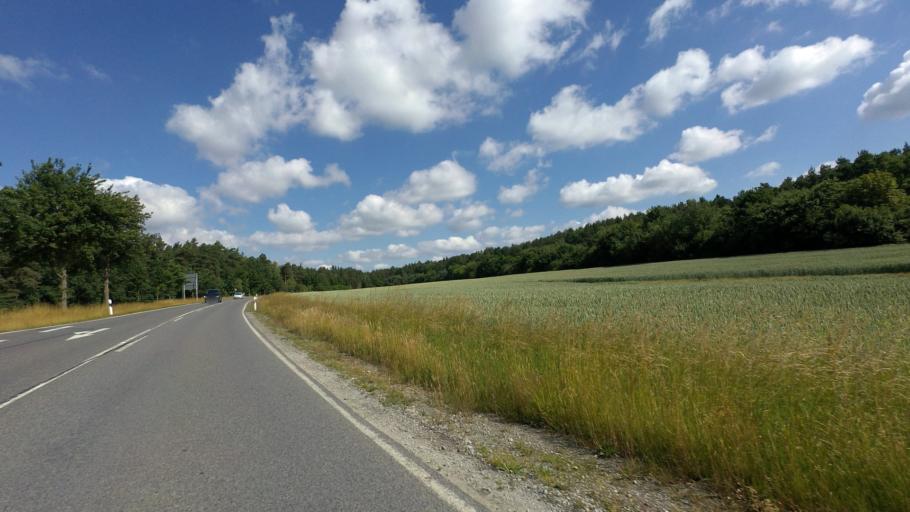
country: DE
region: Saxony
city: Kamenz
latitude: 51.3036
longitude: 14.0946
